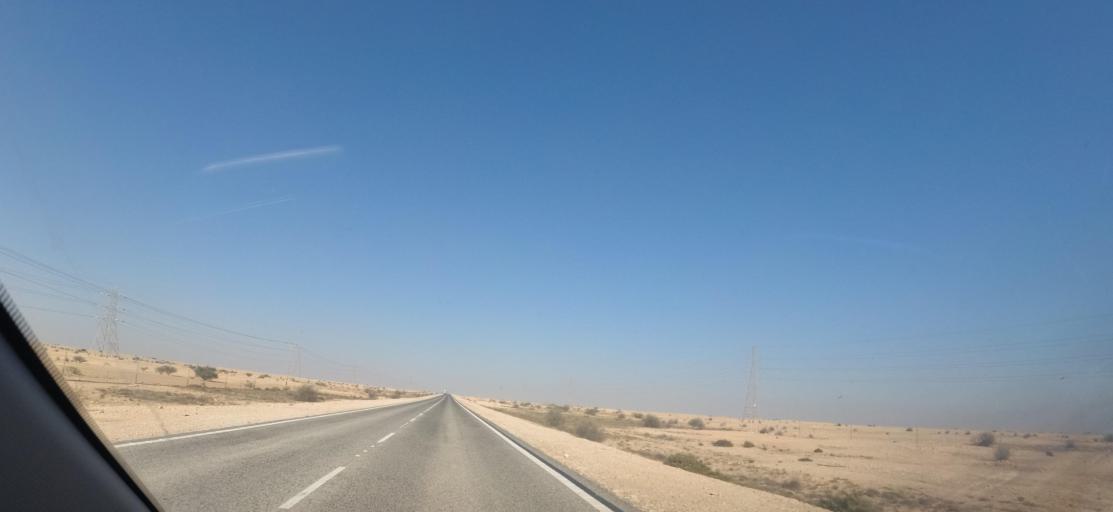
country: QA
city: Al Jumayliyah
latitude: 25.6785
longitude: 51.1345
